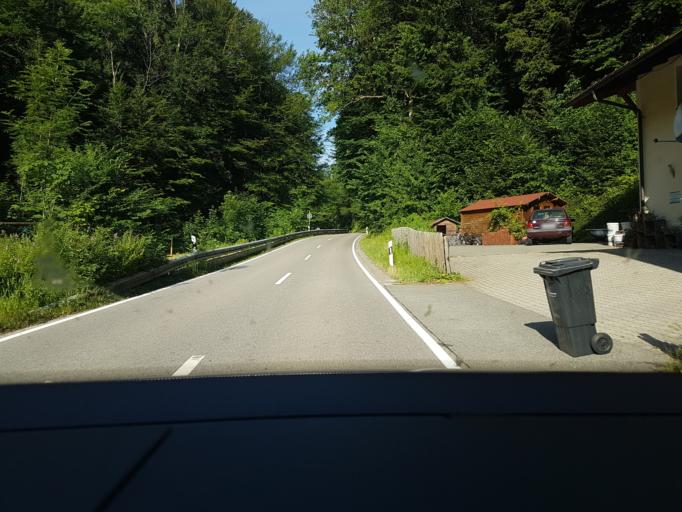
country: DE
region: Bavaria
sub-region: Upper Bavaria
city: Teisendorf
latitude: 47.8344
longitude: 12.7721
